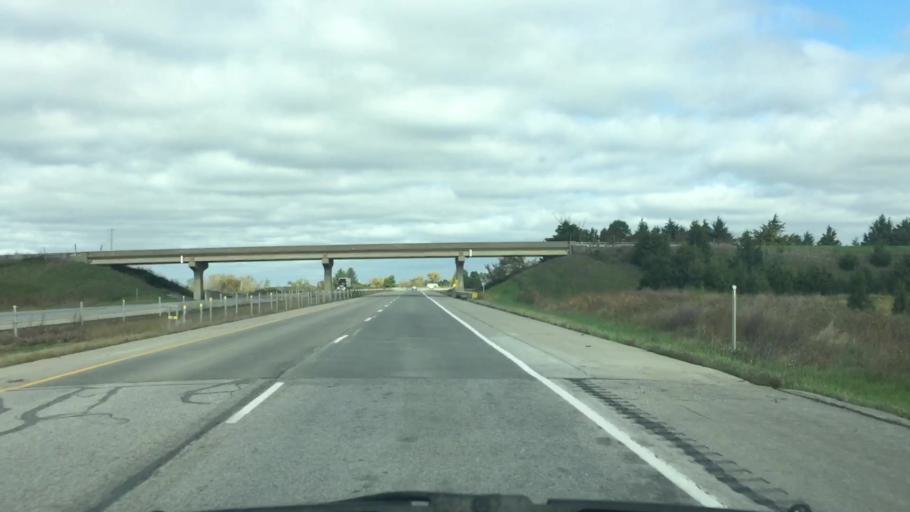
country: US
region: Iowa
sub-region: Clarke County
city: Osceola
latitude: 41.1318
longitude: -93.7854
